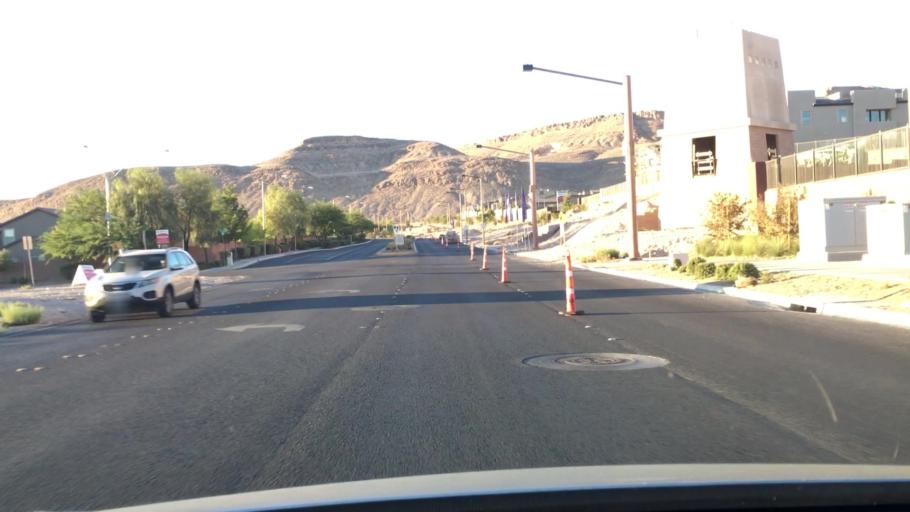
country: US
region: Nevada
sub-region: Clark County
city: Summerlin South
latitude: 36.0705
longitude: -115.3159
